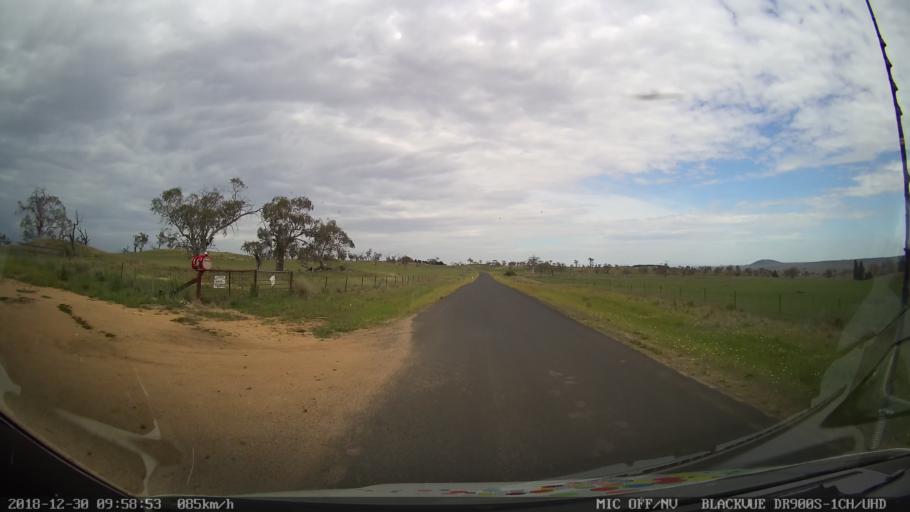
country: AU
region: New South Wales
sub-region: Cooma-Monaro
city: Cooma
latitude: -36.5224
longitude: 149.2193
